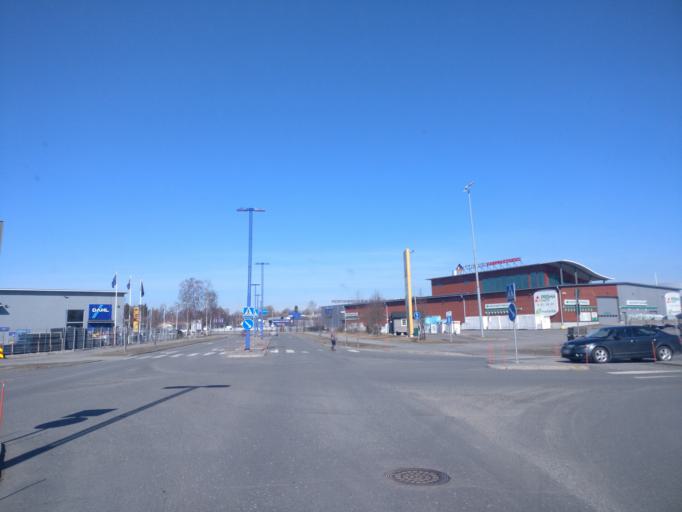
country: FI
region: Lapland
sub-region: Kemi-Tornio
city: Kemi
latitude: 65.7409
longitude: 24.5770
